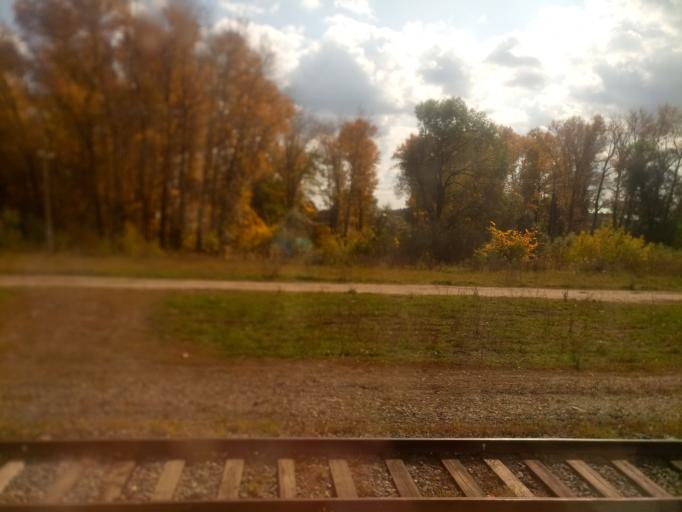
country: RU
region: Chuvashia
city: Urmary
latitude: 55.6875
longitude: 47.9471
